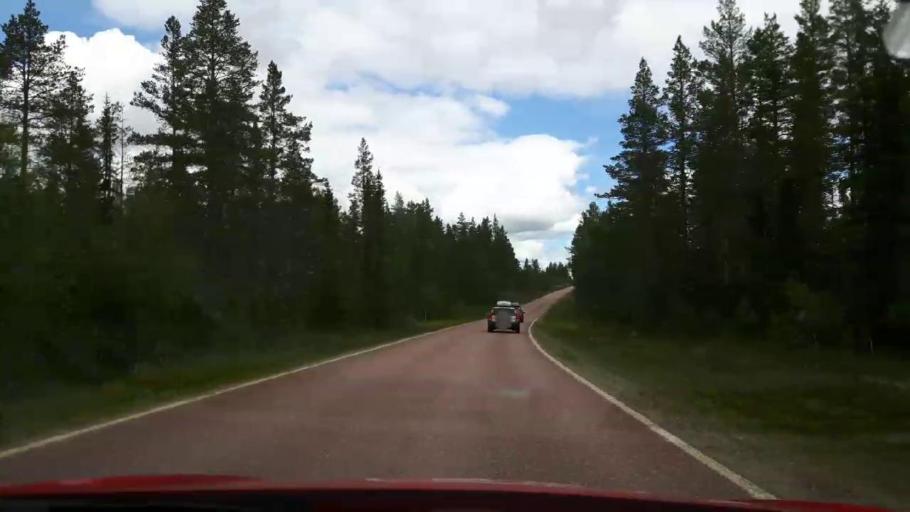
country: NO
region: Hedmark
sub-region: Trysil
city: Innbygda
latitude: 61.8656
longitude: 12.9535
